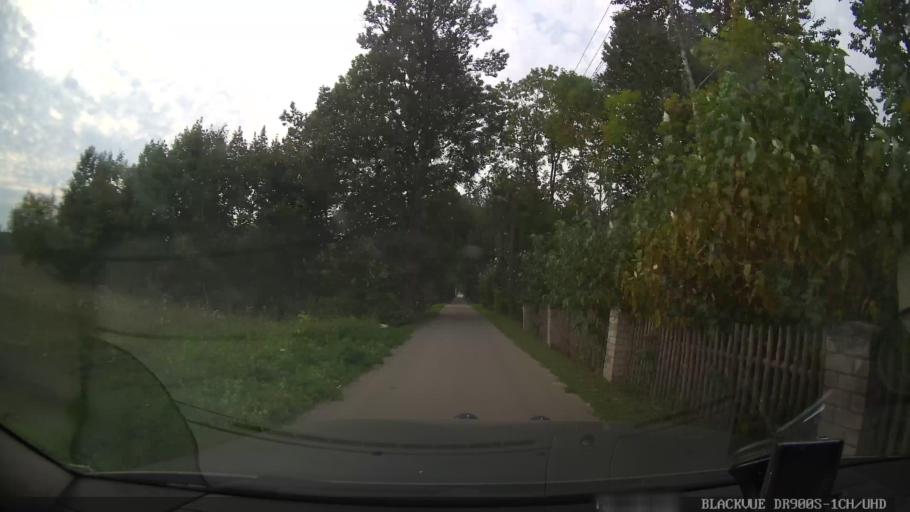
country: BY
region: Grodnenskaya
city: Ashmyany
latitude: 54.5322
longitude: 25.6664
